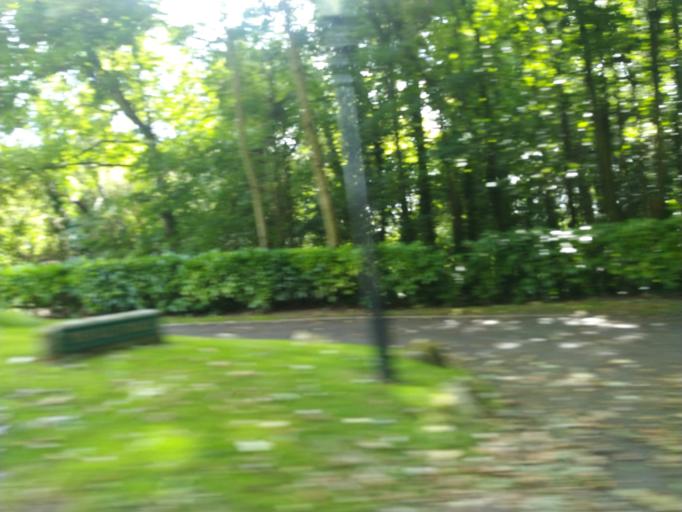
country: GB
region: England
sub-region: Dorset
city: Blandford Forum
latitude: 50.8506
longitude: -2.1414
